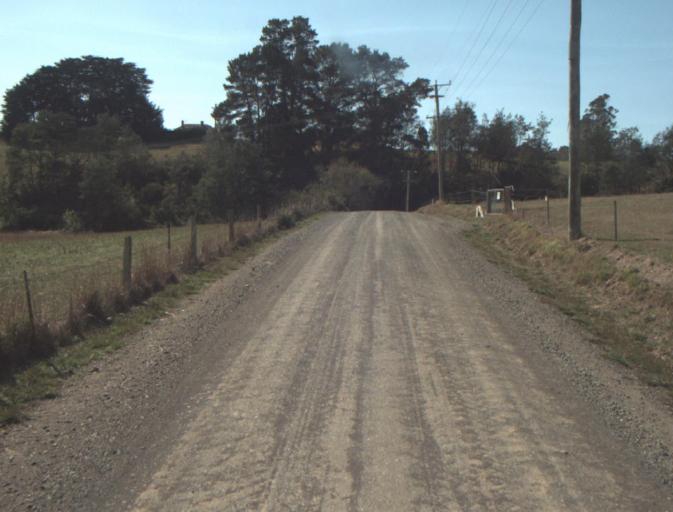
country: AU
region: Tasmania
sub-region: Launceston
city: Mayfield
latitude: -41.2248
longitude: 147.2369
